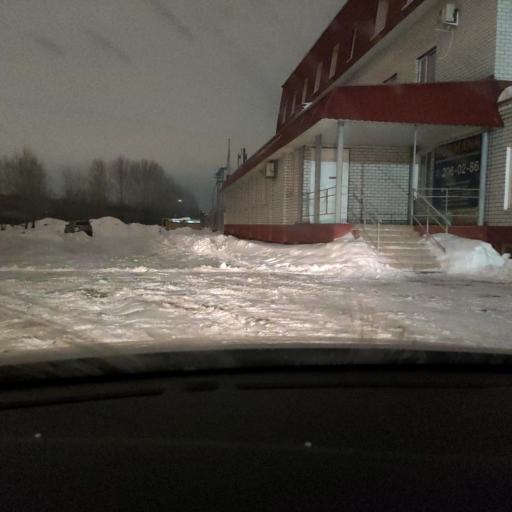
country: RU
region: Tatarstan
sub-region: Gorod Kazan'
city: Kazan
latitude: 55.7692
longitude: 49.0983
